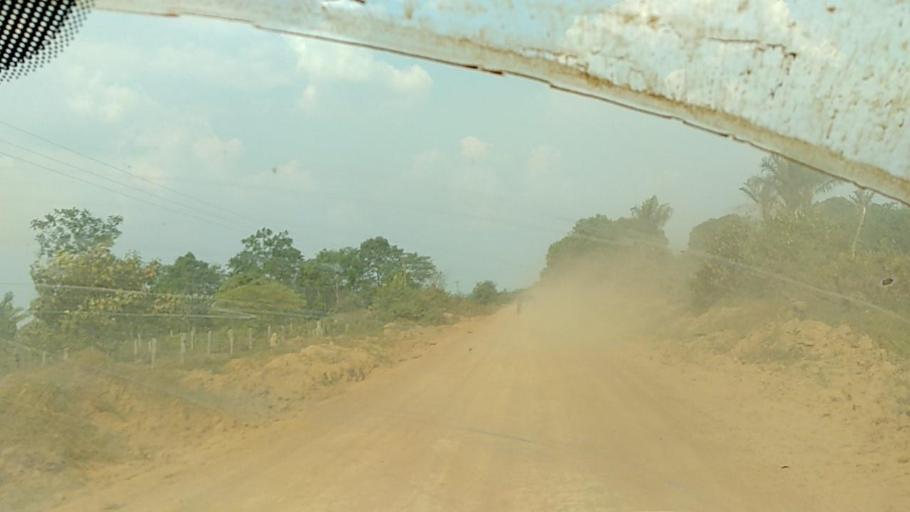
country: BR
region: Rondonia
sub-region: Porto Velho
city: Porto Velho
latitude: -8.6832
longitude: -63.2255
